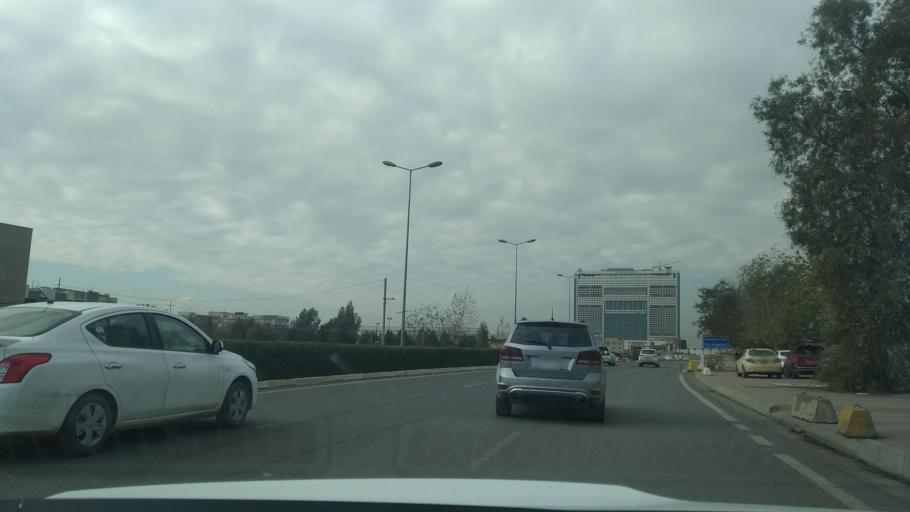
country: IQ
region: Arbil
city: Erbil
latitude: 36.1845
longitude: 43.9904
